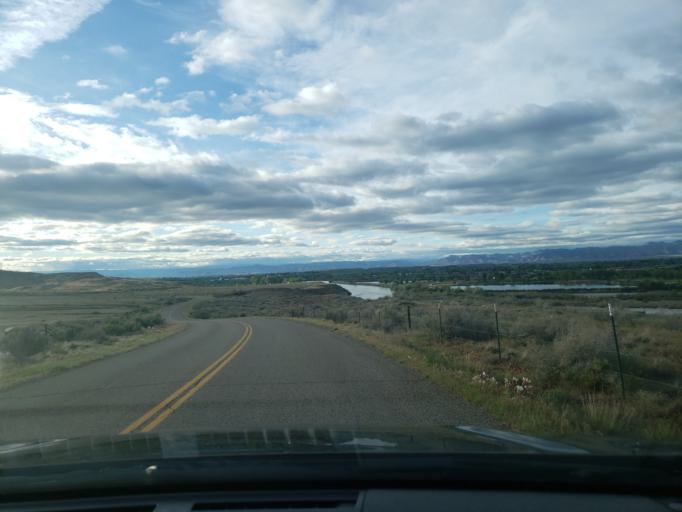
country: US
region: Colorado
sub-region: Mesa County
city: Fruita
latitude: 39.1399
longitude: -108.7424
